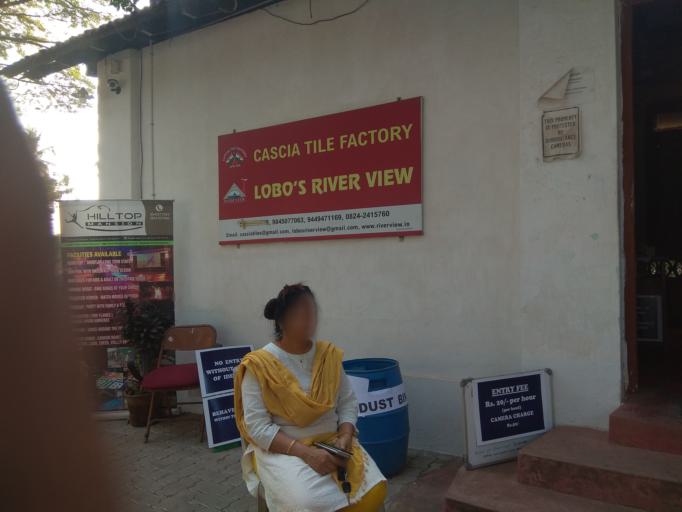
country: IN
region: Karnataka
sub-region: Dakshina Kannada
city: Ullal
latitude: 12.8429
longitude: 74.8507
